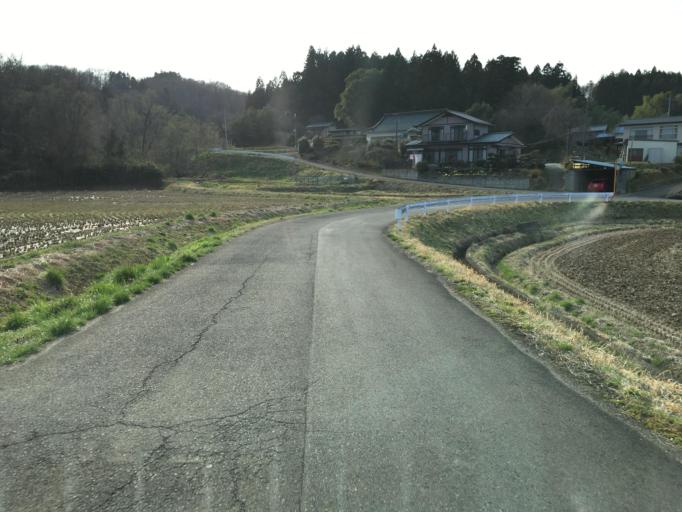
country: JP
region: Fukushima
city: Fukushima-shi
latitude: 37.6650
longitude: 140.4616
